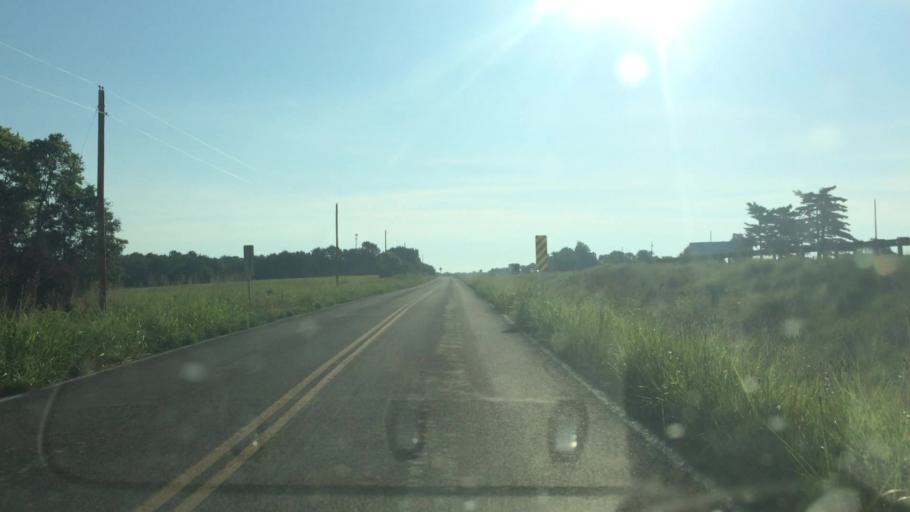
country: US
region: Missouri
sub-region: Greene County
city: Strafford
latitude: 37.2608
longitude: -93.1533
